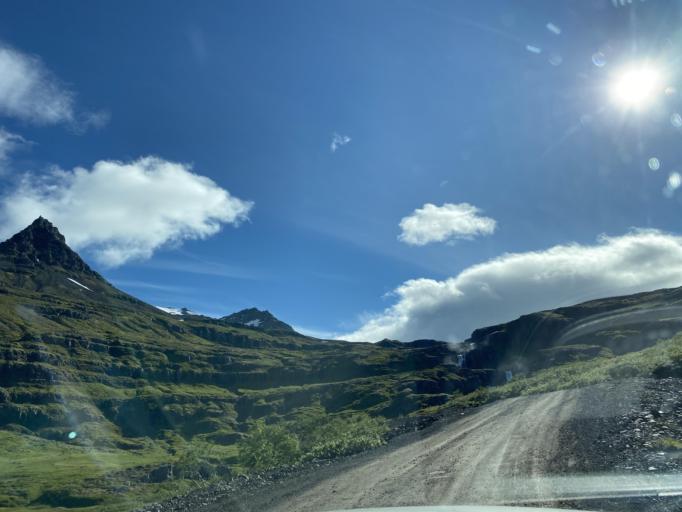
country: IS
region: East
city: Eskifjoerdur
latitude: 65.1816
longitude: -14.0751
